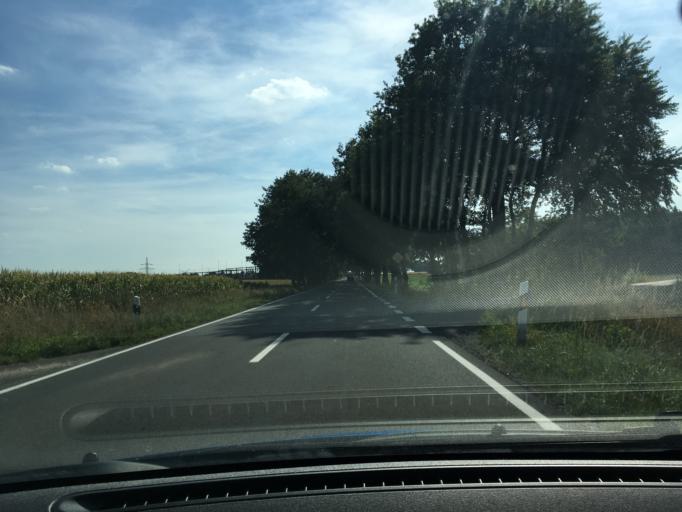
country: DE
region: Lower Saxony
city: Walsrode
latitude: 52.8400
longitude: 9.6450
